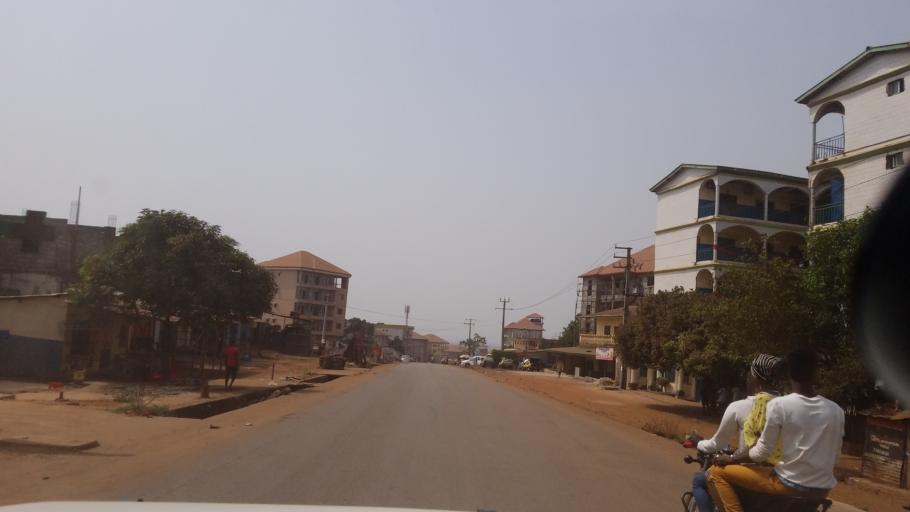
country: GN
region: Kindia
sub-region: Prefecture de Dubreka
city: Dubreka
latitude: 9.6705
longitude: -13.5600
